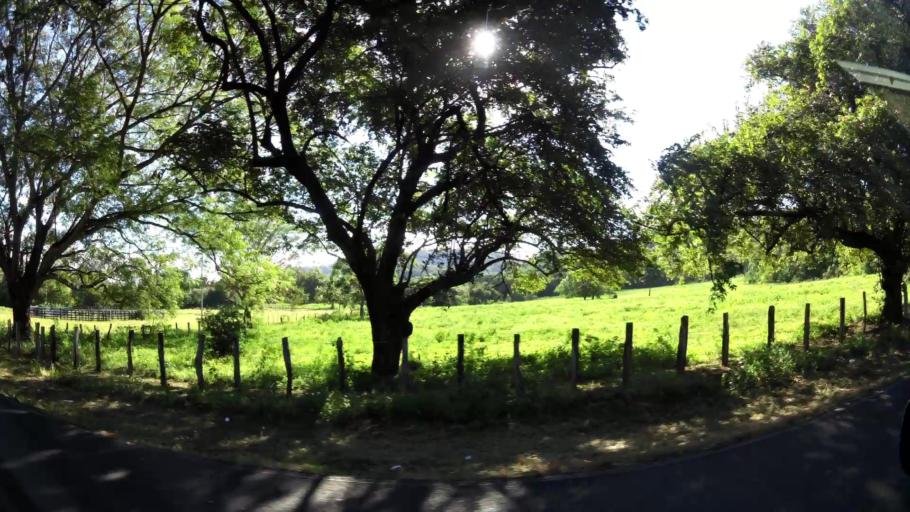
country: CR
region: Guanacaste
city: Belen
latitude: 10.3819
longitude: -85.6204
